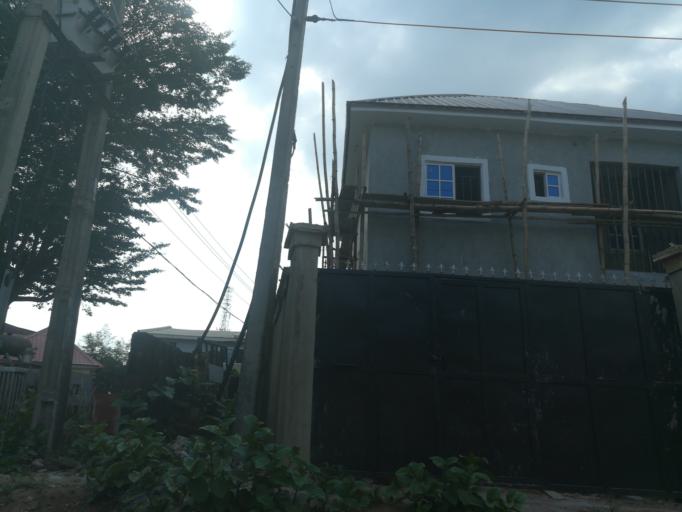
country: NG
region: Abuja Federal Capital Territory
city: Abuja
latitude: 9.0810
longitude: 7.4137
